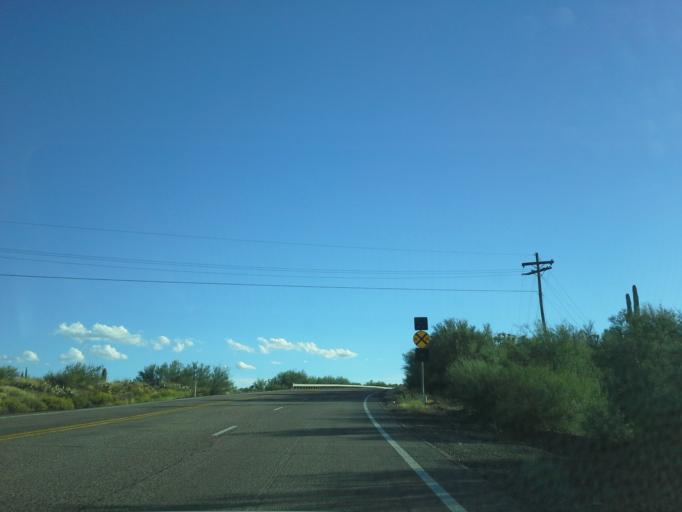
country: US
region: Arizona
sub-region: Pinal County
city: Mammoth
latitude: 32.6973
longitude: -110.6442
